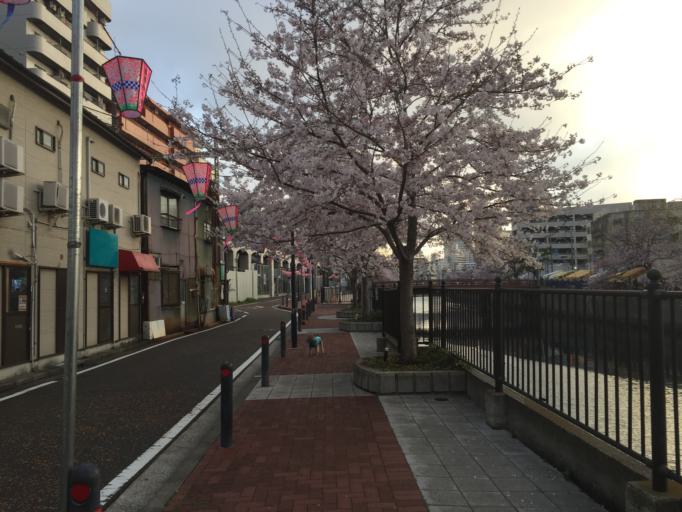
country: JP
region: Kanagawa
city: Yokohama
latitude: 35.4428
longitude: 139.6264
